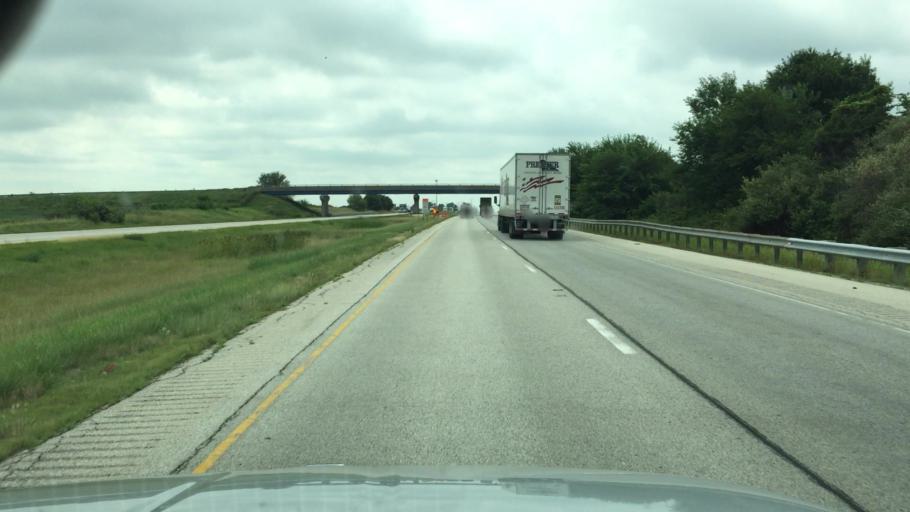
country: US
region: Illinois
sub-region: Knox County
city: Galesburg
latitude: 41.0075
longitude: -90.3351
